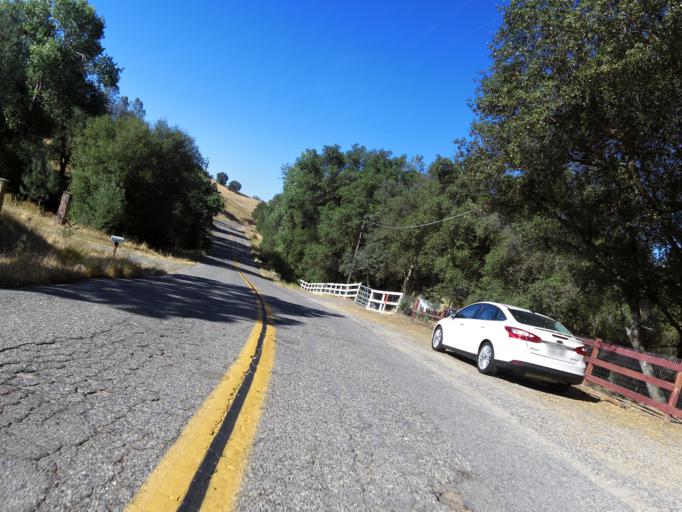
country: US
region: California
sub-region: Madera County
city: Yosemite Lakes
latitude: 37.1842
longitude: -119.8266
